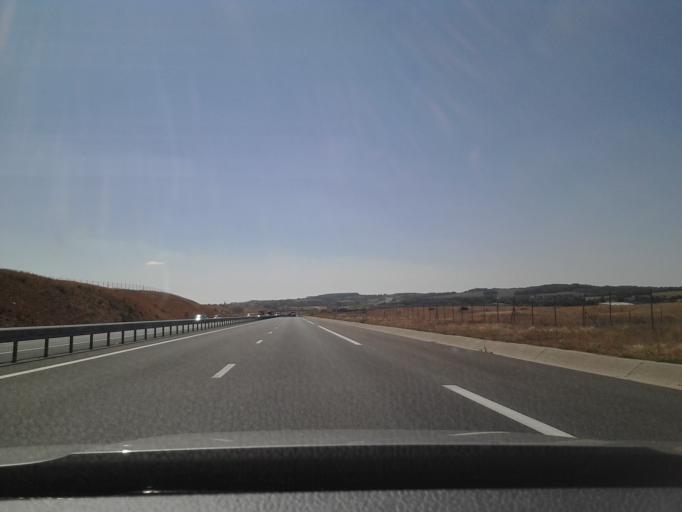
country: FR
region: Midi-Pyrenees
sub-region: Departement de l'Aveyron
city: La Cavalerie
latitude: 44.0216
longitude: 3.1239
